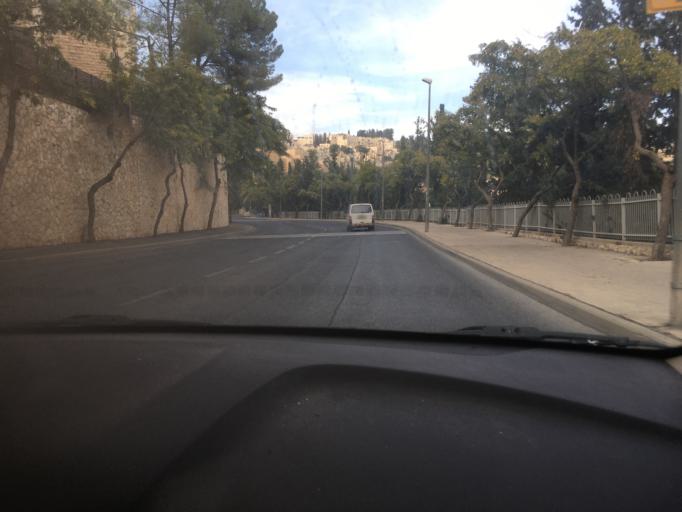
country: PS
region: West Bank
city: Ash Shaykh Sa`d
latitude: 31.7478
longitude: 35.2331
